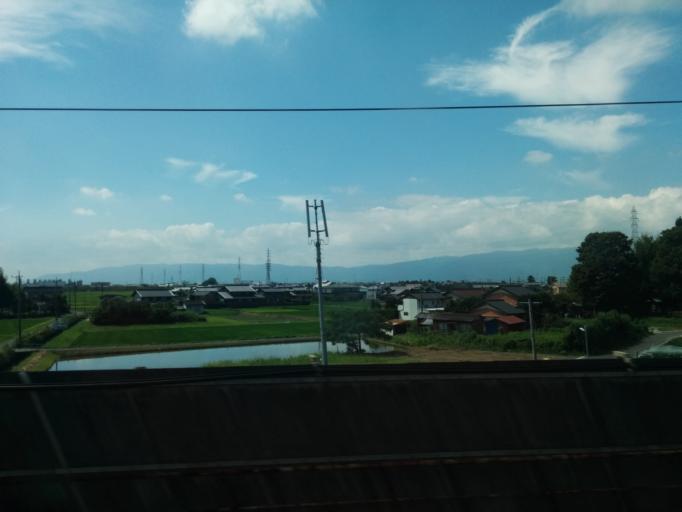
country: JP
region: Gifu
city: Ogaki
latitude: 35.3385
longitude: 136.6555
